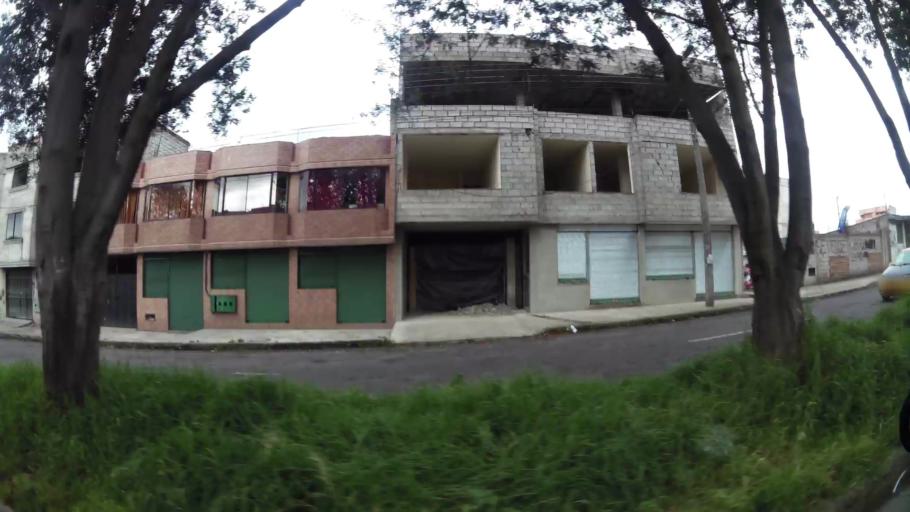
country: EC
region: Pichincha
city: Quito
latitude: -0.3136
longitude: -78.5532
